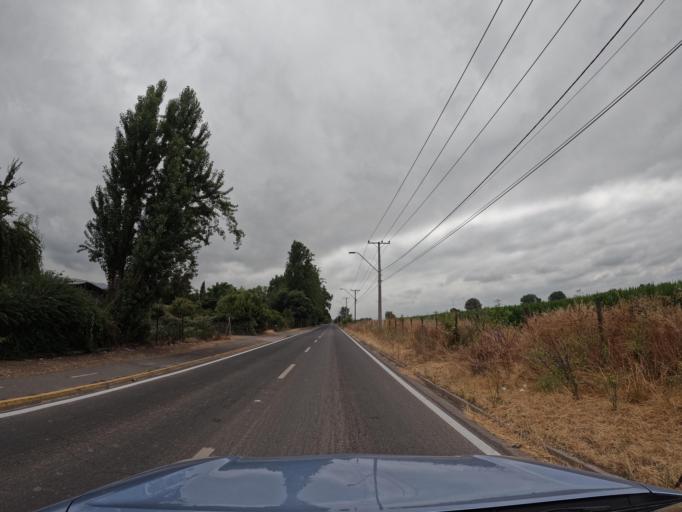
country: CL
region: O'Higgins
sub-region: Provincia de Colchagua
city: Chimbarongo
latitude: -34.7326
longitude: -71.0616
